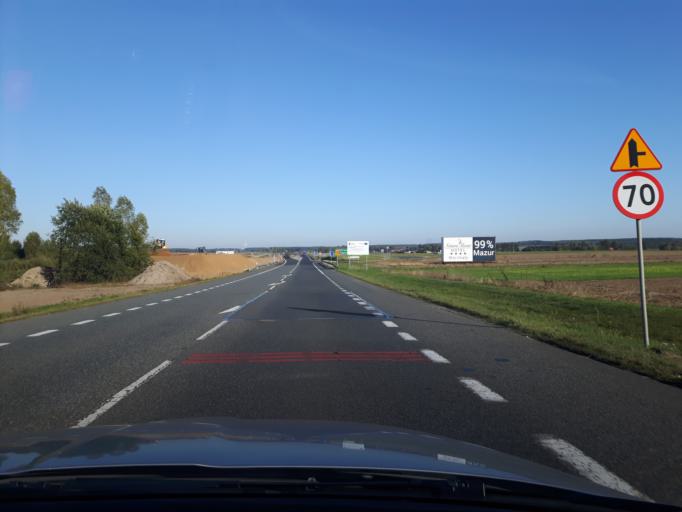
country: PL
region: Masovian Voivodeship
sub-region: Powiat mlawski
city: Wieczfnia Koscielna
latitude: 53.2116
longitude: 20.4312
